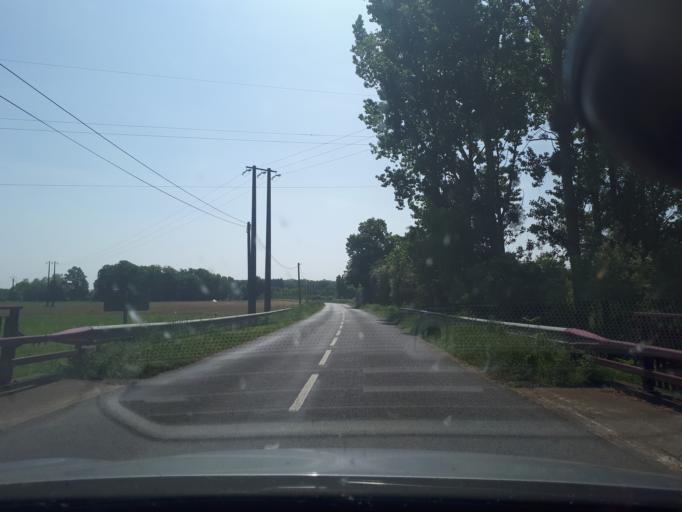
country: FR
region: Pays de la Loire
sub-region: Departement de la Sarthe
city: Champagne
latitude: 48.0792
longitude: 0.3246
